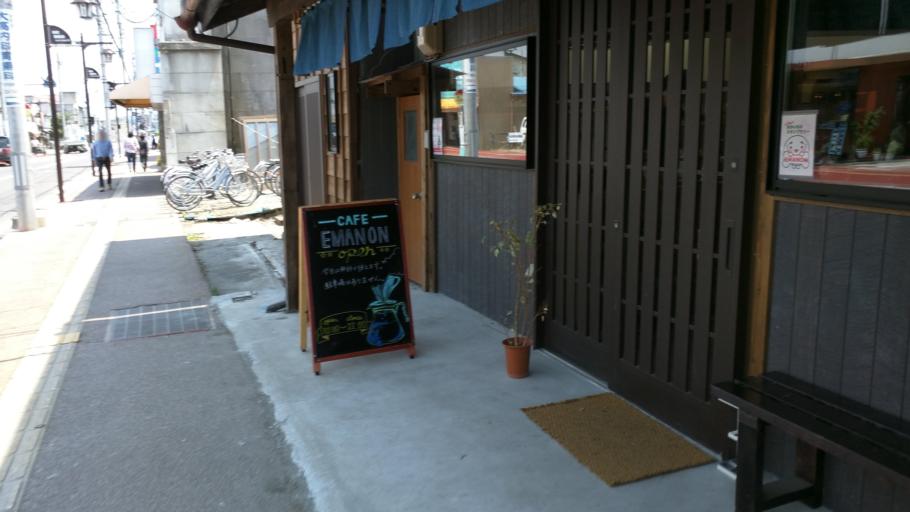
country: JP
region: Fukushima
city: Sukagawa
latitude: 37.1267
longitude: 140.2158
